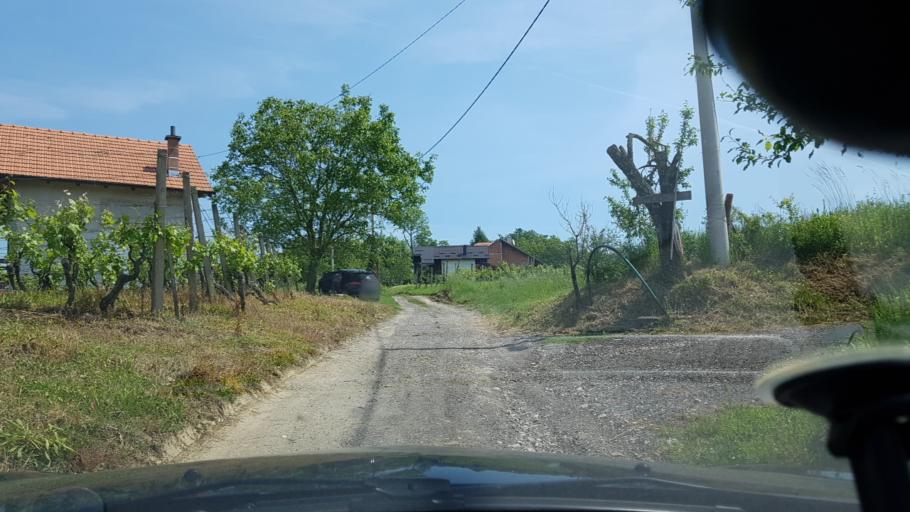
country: HR
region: Krapinsko-Zagorska
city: Marija Bistrica
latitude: 45.9380
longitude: 16.2103
